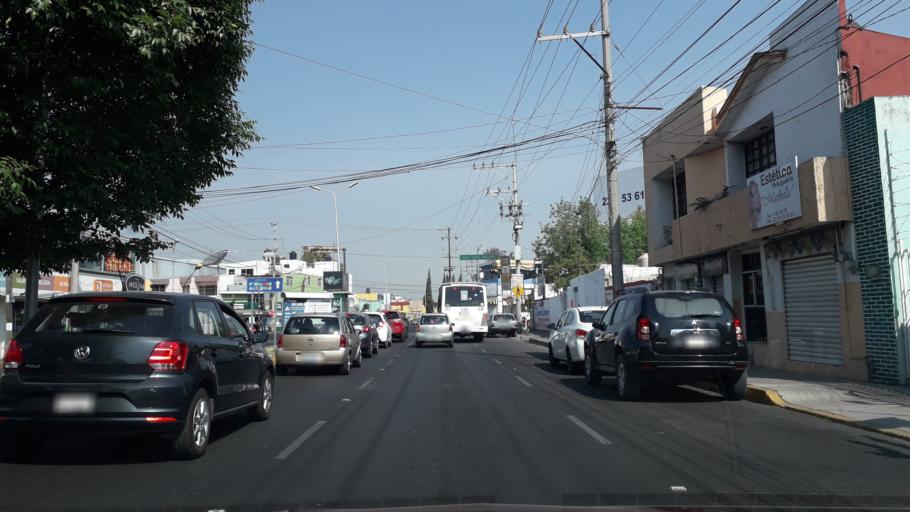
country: MX
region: Puebla
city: Puebla
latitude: 19.0692
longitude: -98.2192
